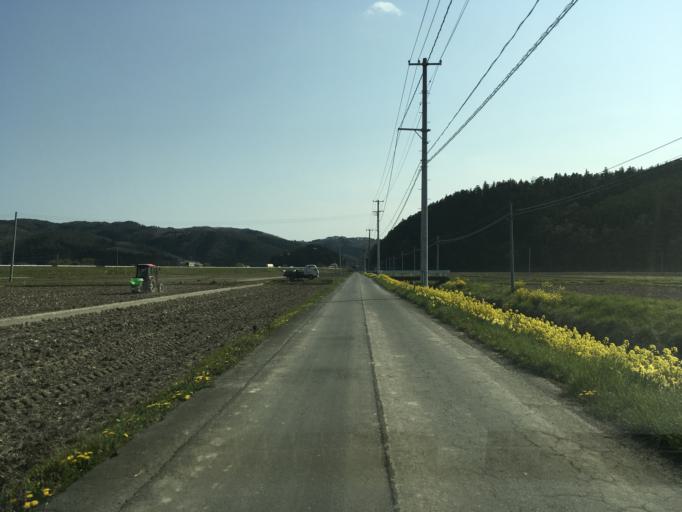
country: JP
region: Iwate
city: Ichinoseki
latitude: 38.7553
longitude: 141.3234
